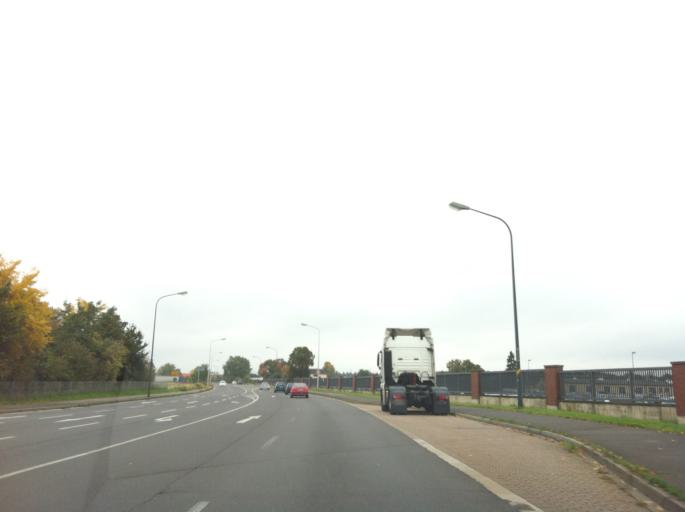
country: DE
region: North Rhine-Westphalia
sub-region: Regierungsbezirk Koln
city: Dueren
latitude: 50.7884
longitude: 6.5042
